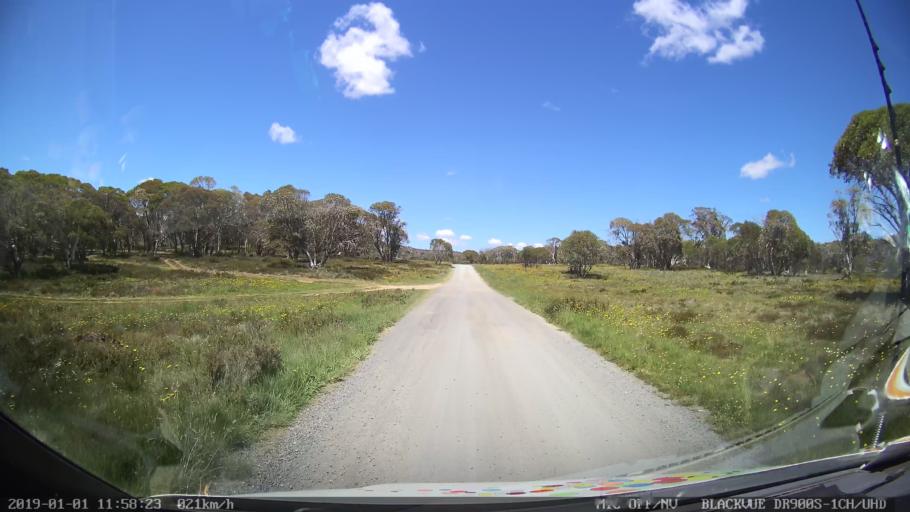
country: AU
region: New South Wales
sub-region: Snowy River
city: Jindabyne
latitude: -35.8897
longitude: 148.4483
